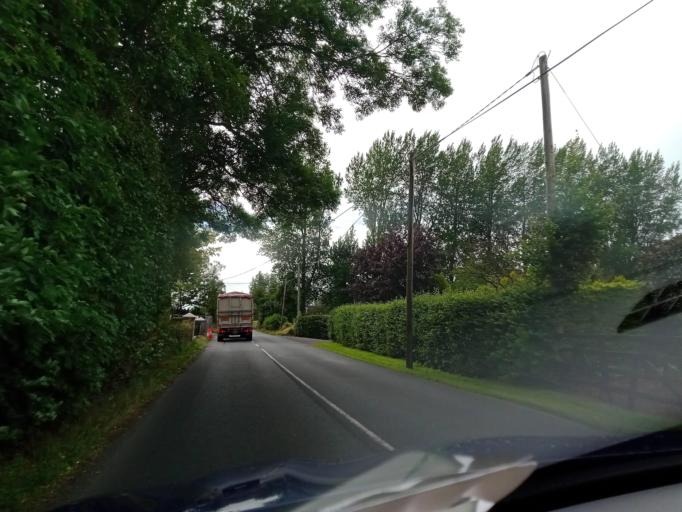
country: IE
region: Leinster
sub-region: Laois
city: Portlaoise
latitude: 53.0170
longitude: -7.2925
